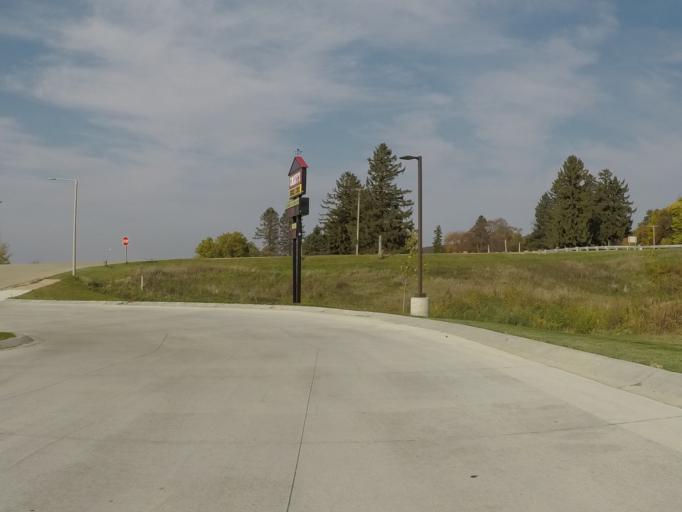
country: US
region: Wisconsin
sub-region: Iowa County
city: Barneveld
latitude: 43.0134
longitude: -89.8233
